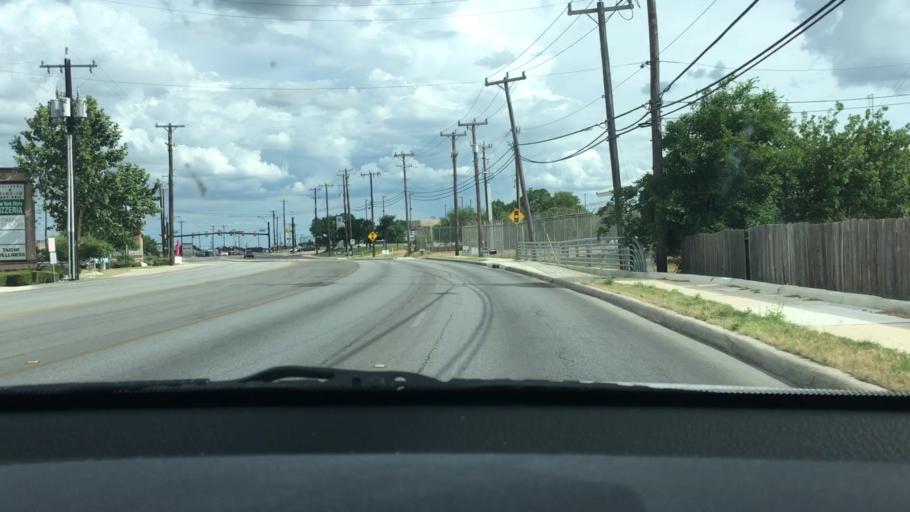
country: US
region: Texas
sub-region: Bexar County
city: Timberwood Park
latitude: 29.6497
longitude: -98.4262
